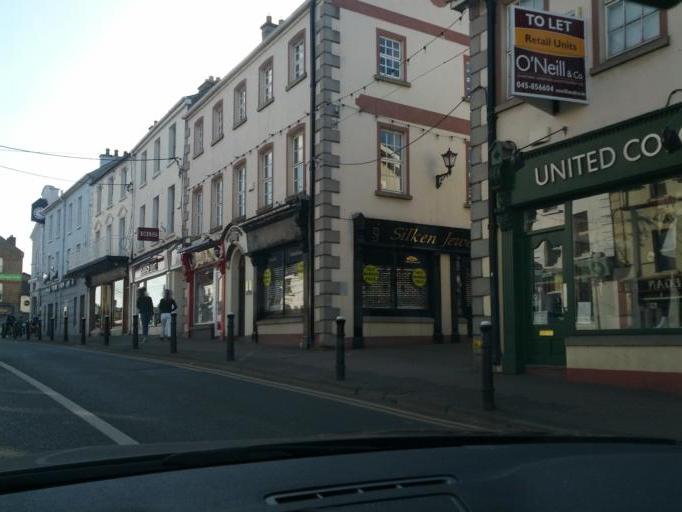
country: IE
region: Leinster
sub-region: Kildare
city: Naas
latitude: 53.2187
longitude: -6.6629
